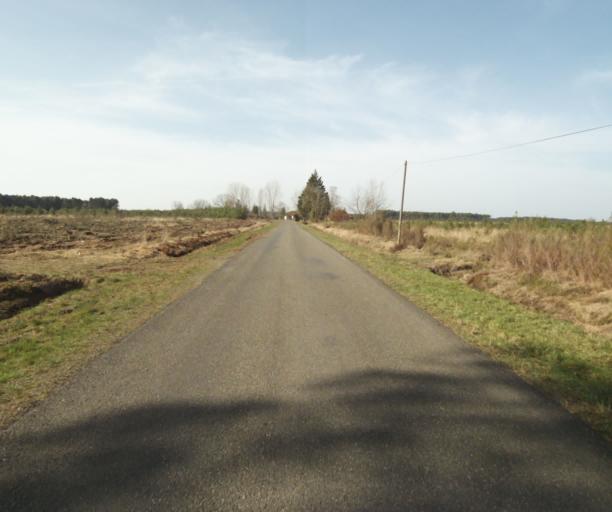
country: FR
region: Aquitaine
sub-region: Departement des Landes
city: Roquefort
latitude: 44.1843
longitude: -0.2305
